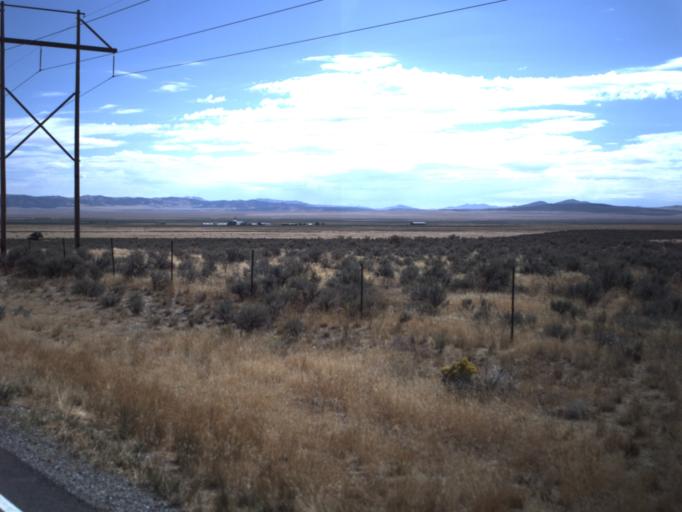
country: US
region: Idaho
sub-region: Oneida County
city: Malad City
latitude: 41.9658
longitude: -112.9942
